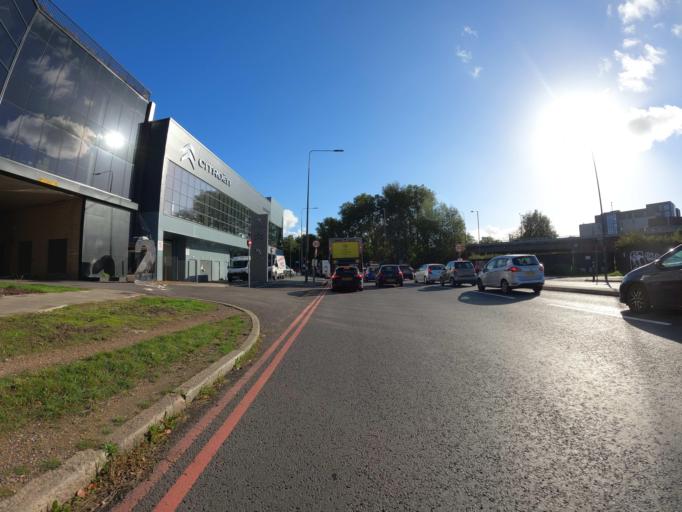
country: GB
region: England
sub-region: Greater London
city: Acton
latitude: 51.4926
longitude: -0.2820
